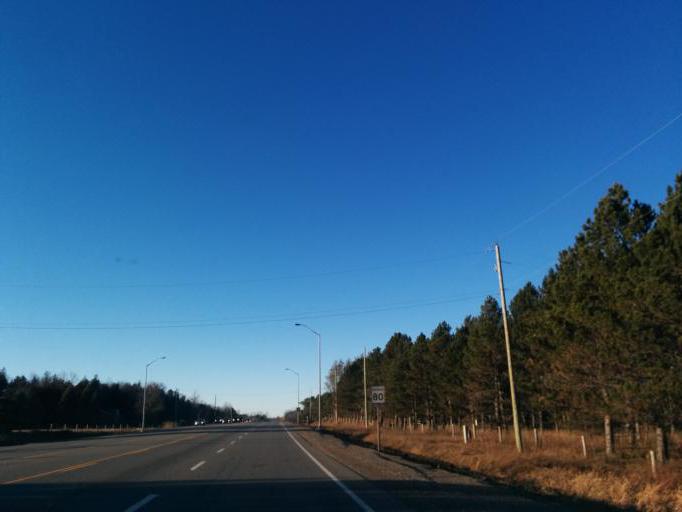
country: CA
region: Ontario
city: Orangeville
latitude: 43.9024
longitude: -80.0532
